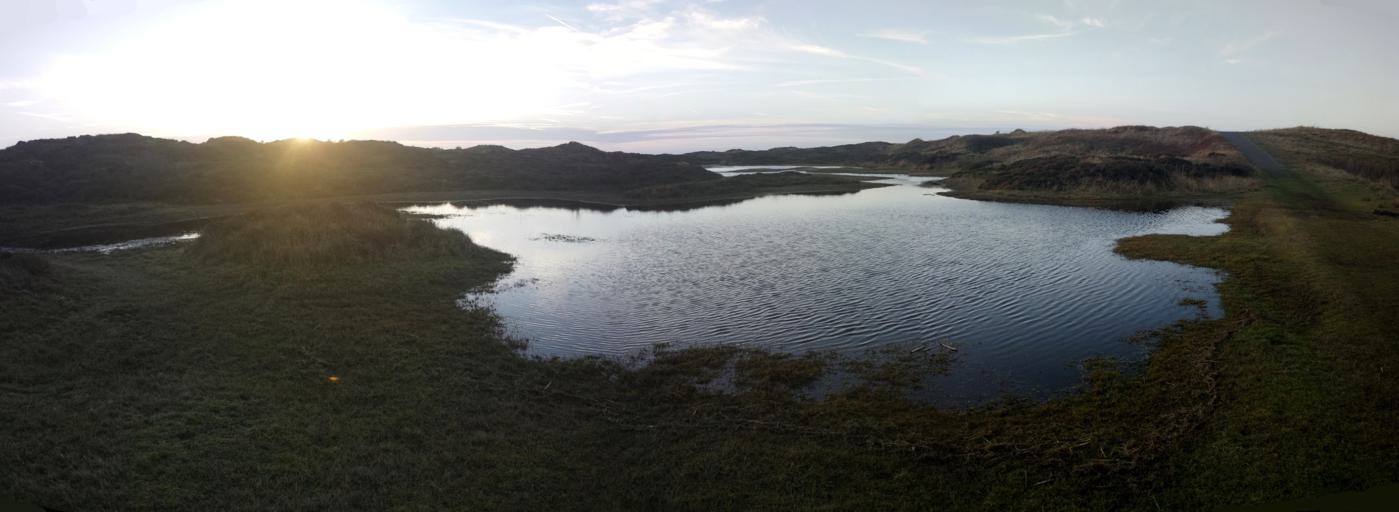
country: NL
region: North Holland
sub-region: Gemeente Den Helder
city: Den Helder
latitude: 53.0126
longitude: 4.7408
